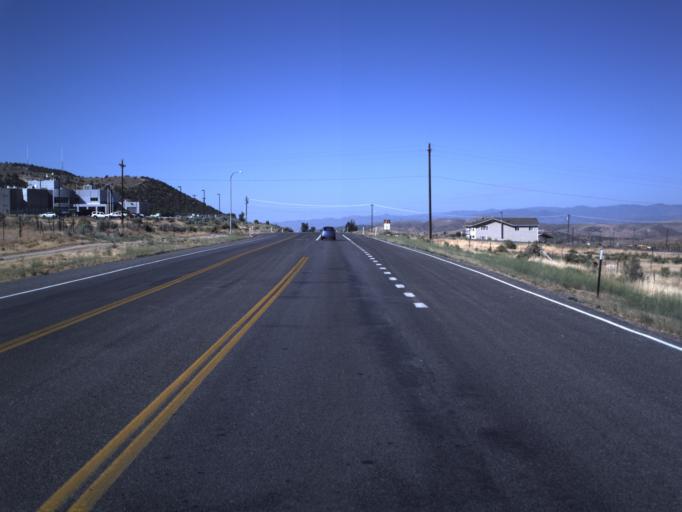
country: US
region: Utah
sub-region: Sanpete County
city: Manti
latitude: 39.2506
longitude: -111.6434
